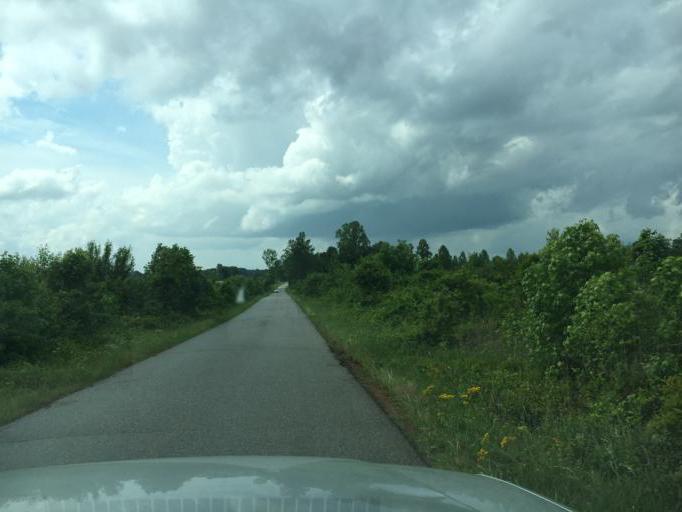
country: US
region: South Carolina
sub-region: Spartanburg County
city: Fairforest
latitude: 34.9245
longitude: -82.0537
